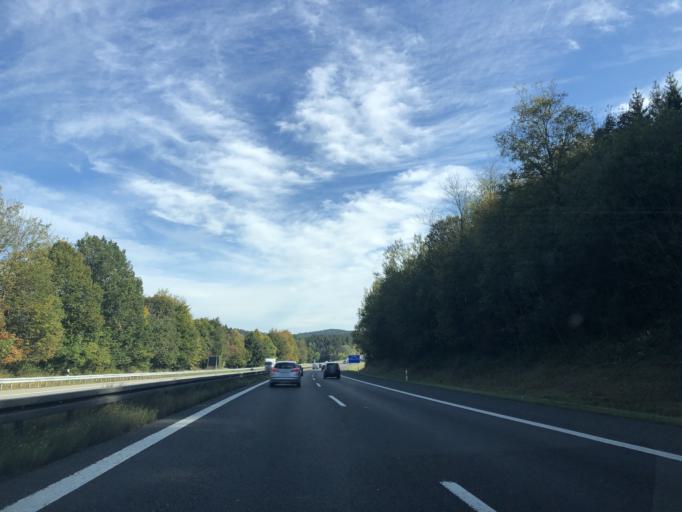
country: DE
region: Bavaria
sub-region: Upper Palatinate
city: Lupburg
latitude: 49.1769
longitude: 11.7595
